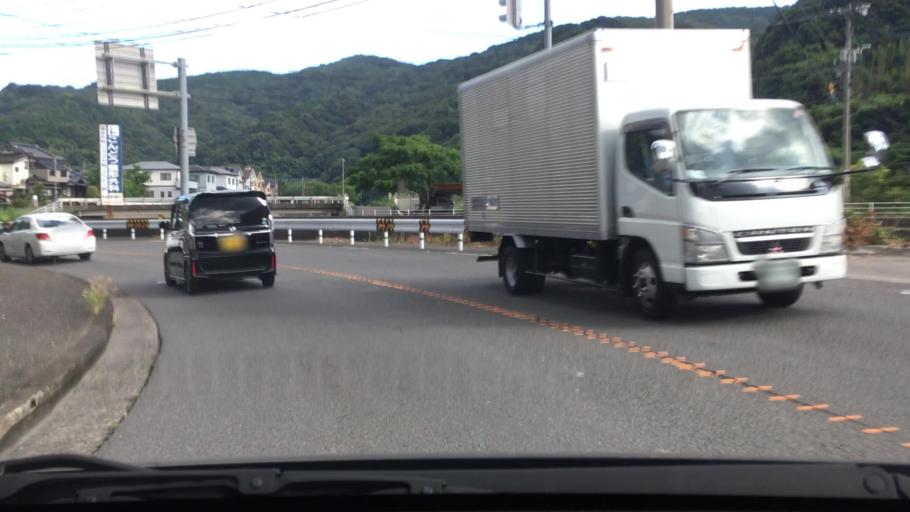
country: JP
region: Nagasaki
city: Togitsu
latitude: 32.8260
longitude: 129.7845
